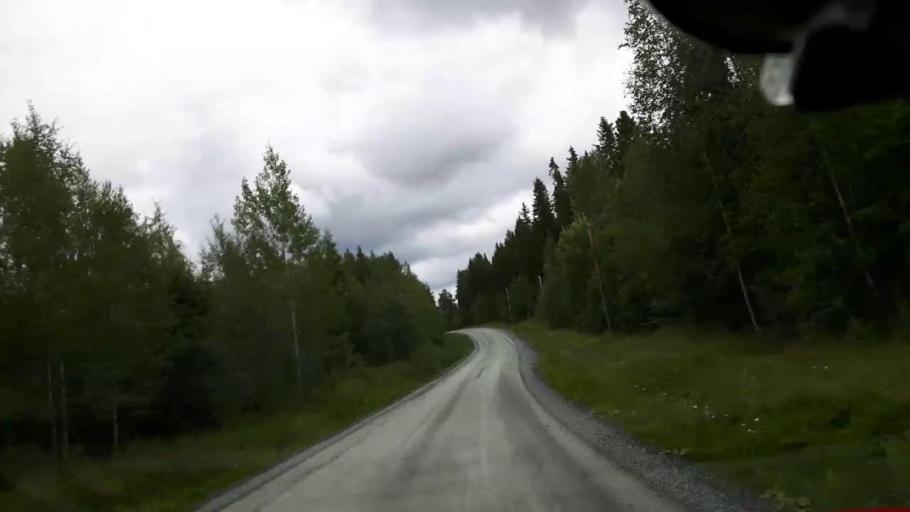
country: SE
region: Jaemtland
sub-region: Krokoms Kommun
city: Krokom
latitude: 63.5778
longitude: 14.2224
